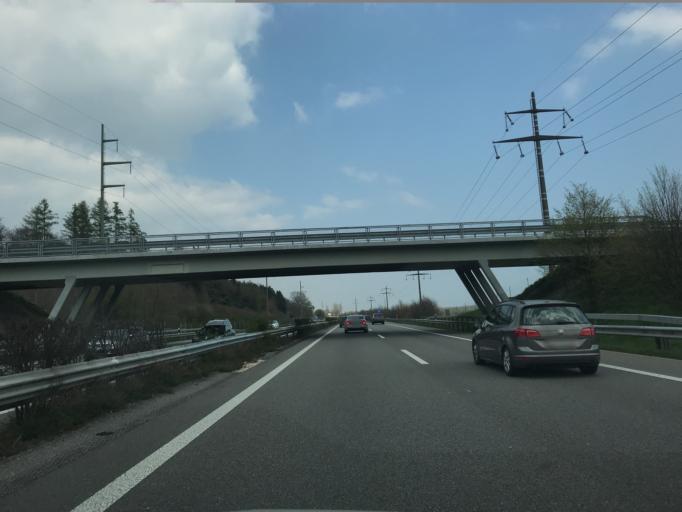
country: CH
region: Vaud
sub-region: Nyon District
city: Founex
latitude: 46.3609
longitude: 6.1849
